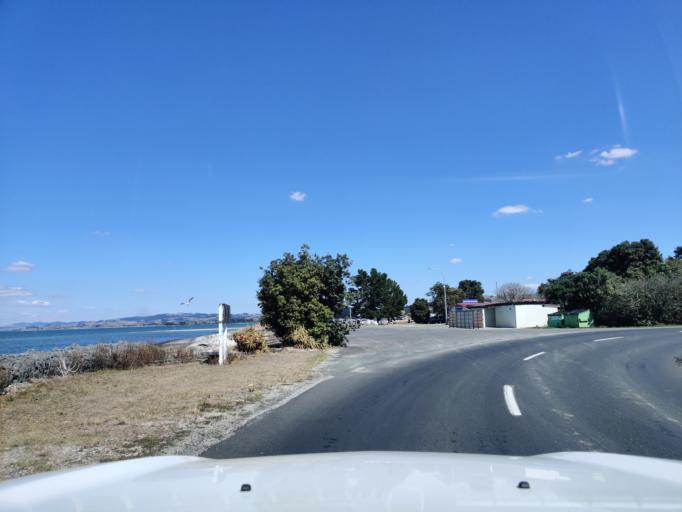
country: NZ
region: Waikato
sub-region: Thames-Coromandel District
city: Thames
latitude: -37.1089
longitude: 175.2989
